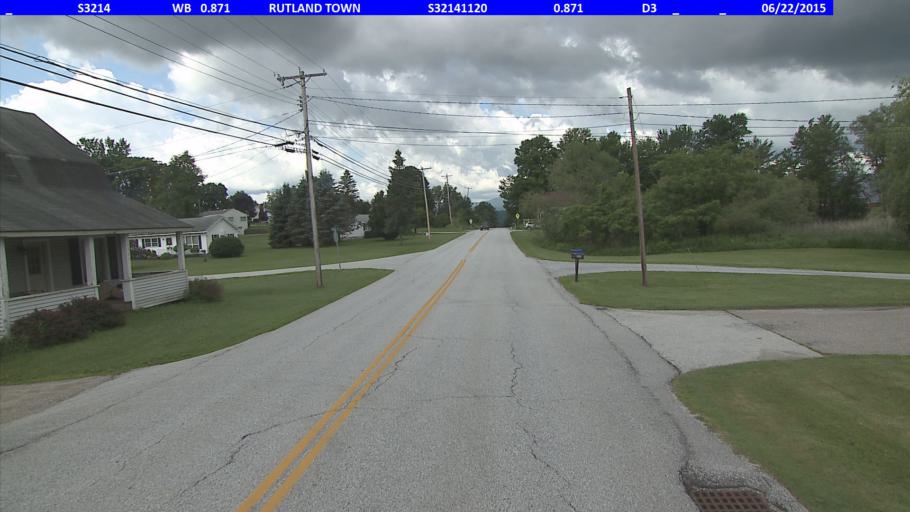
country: US
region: Vermont
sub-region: Rutland County
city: Rutland
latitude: 43.6391
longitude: -72.9609
